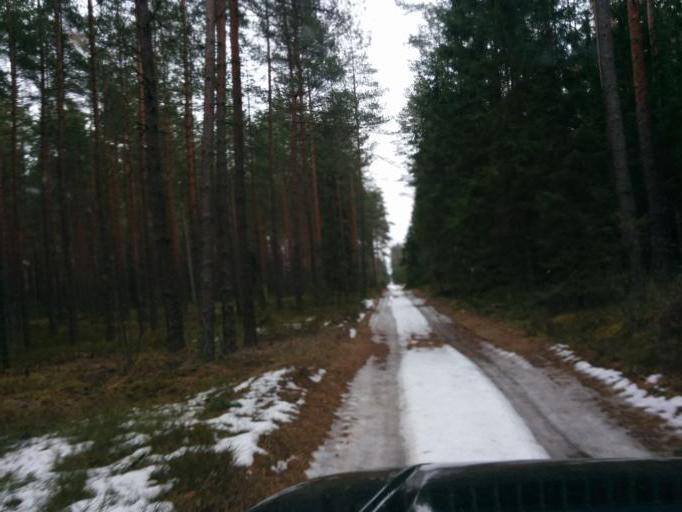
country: LV
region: Ogre
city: Ogre
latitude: 56.7497
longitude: 24.5799
